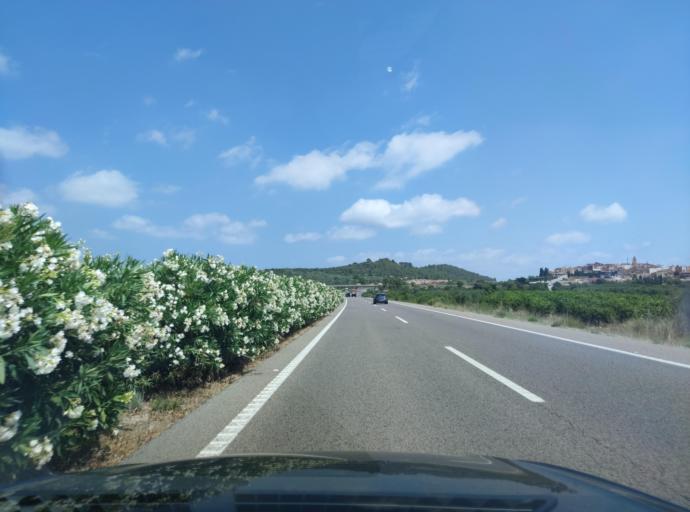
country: ES
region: Catalonia
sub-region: Provincia de Tarragona
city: Masdenverge
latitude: 40.6658
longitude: 0.5133
